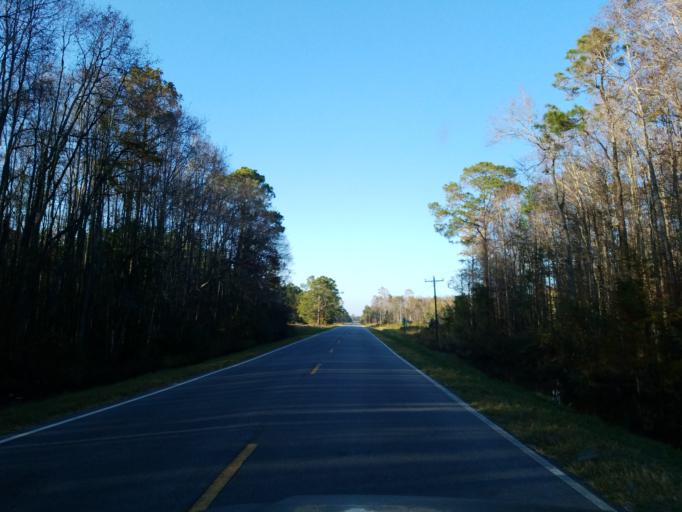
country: US
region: Georgia
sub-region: Lanier County
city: Lakeland
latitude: 31.1158
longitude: -83.0826
